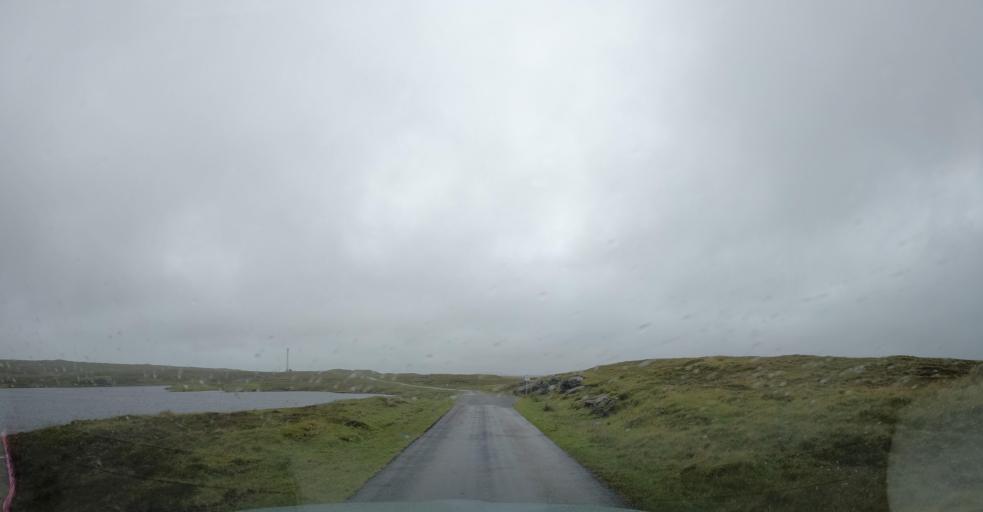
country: GB
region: Scotland
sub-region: Eilean Siar
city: Benbecula
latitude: 57.4926
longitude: -7.2261
